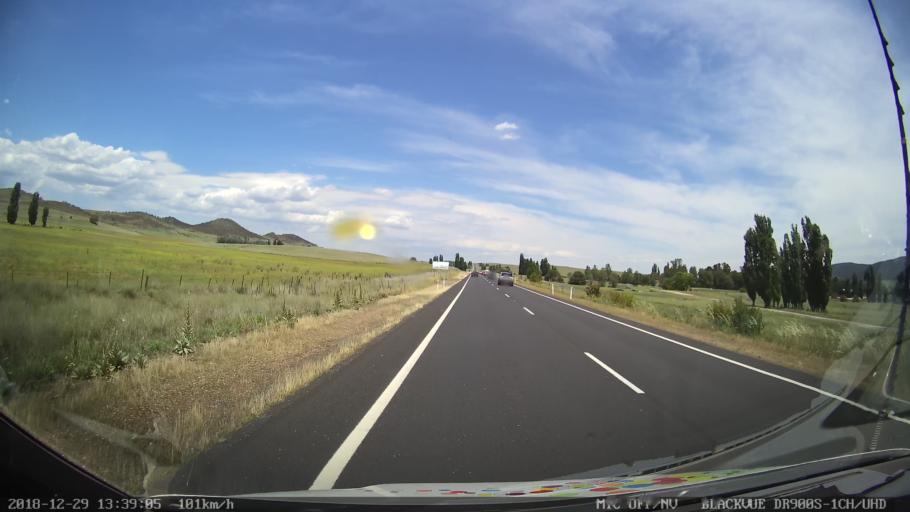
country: AU
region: New South Wales
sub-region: Cooma-Monaro
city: Cooma
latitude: -36.0078
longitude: 149.1451
